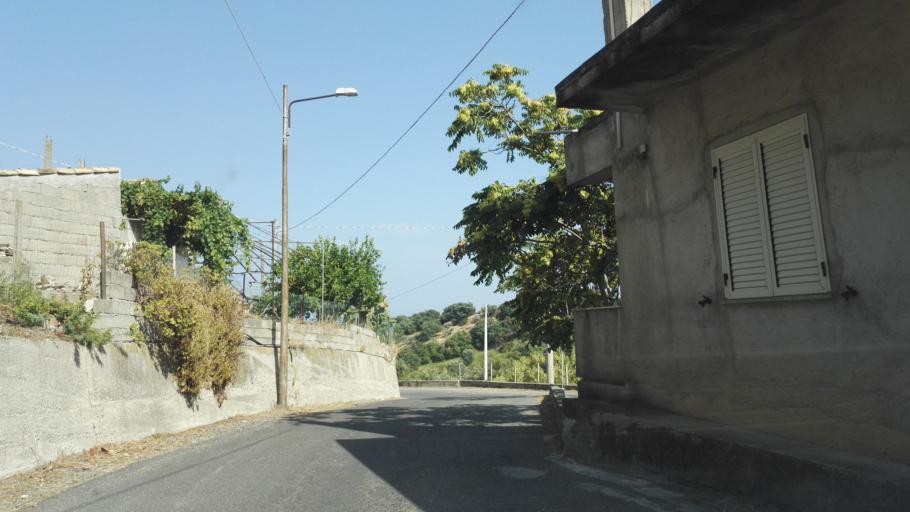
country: IT
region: Calabria
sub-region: Provincia di Reggio Calabria
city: Monasterace
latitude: 38.4526
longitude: 16.5537
